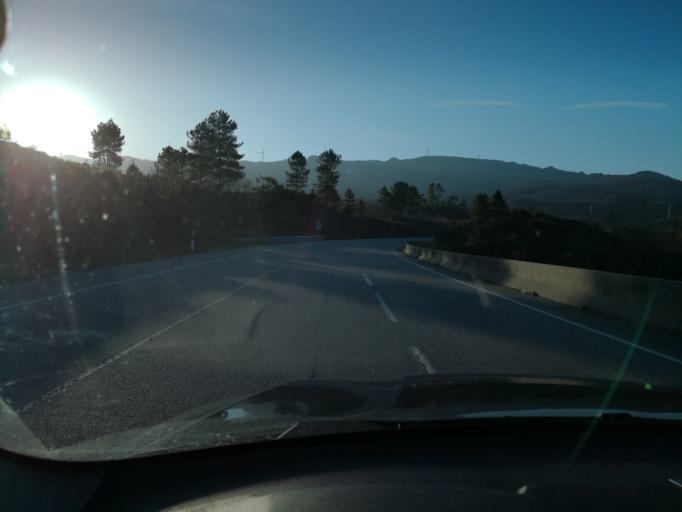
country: PT
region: Vila Real
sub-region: Vila Real
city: Vila Real
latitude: 41.3727
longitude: -7.7126
